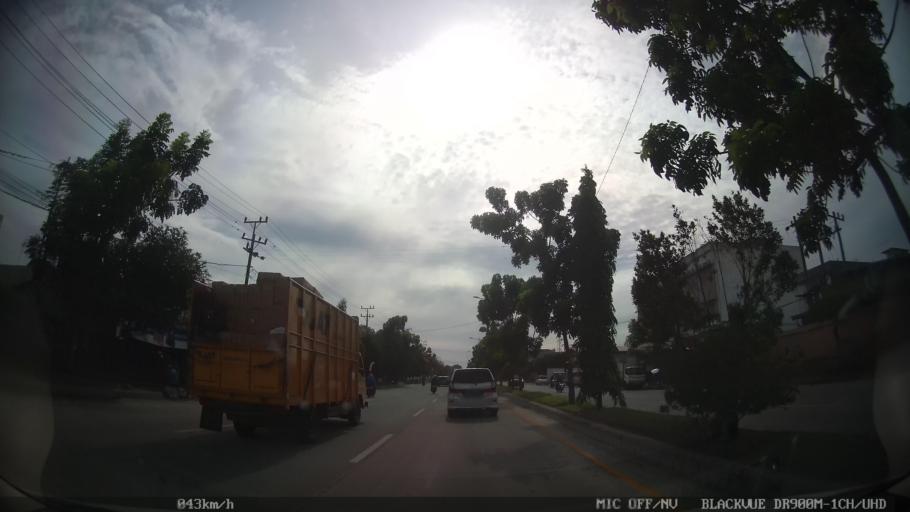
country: ID
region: North Sumatra
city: Medan
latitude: 3.6296
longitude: 98.6862
